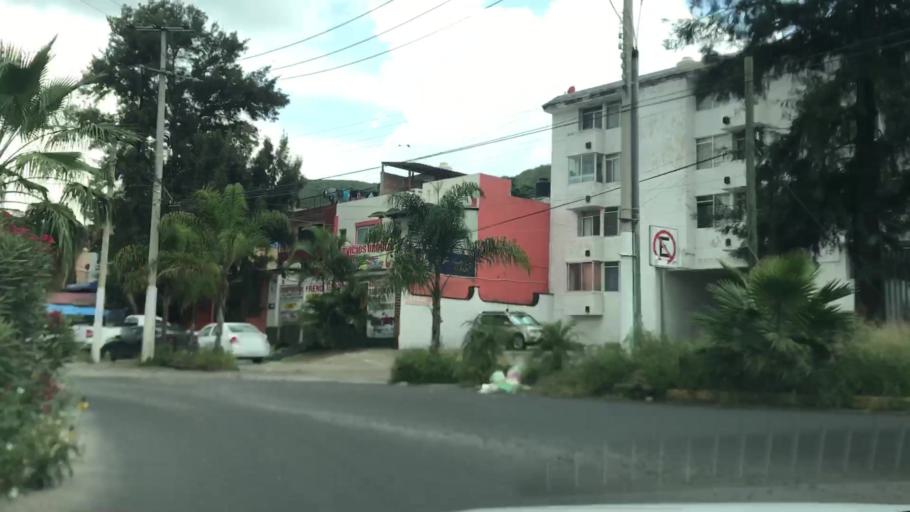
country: MX
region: Jalisco
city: Guadalajara
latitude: 20.6213
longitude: -103.4090
